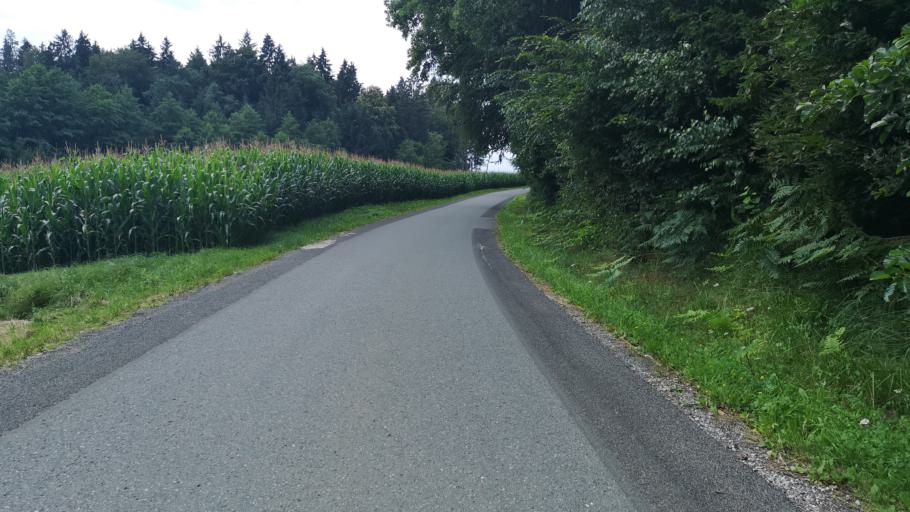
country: AT
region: Styria
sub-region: Politischer Bezirk Leibnitz
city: Weitendorf
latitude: 46.8785
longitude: 15.4659
